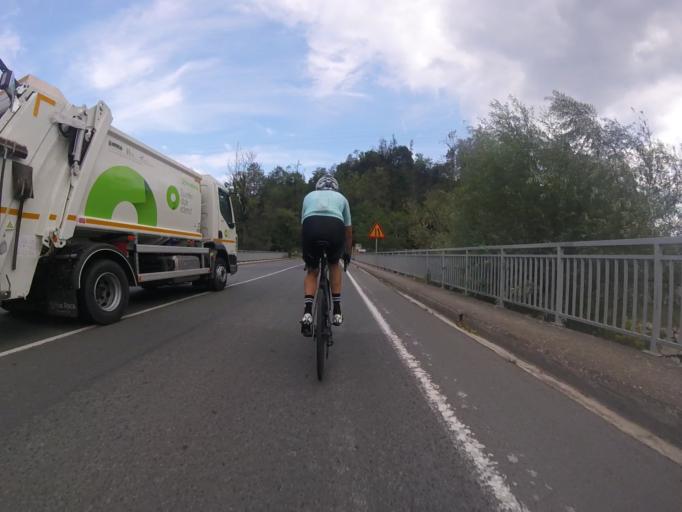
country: ES
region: Basque Country
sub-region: Provincia de Guipuzcoa
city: Aduna
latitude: 43.1974
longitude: -2.0504
